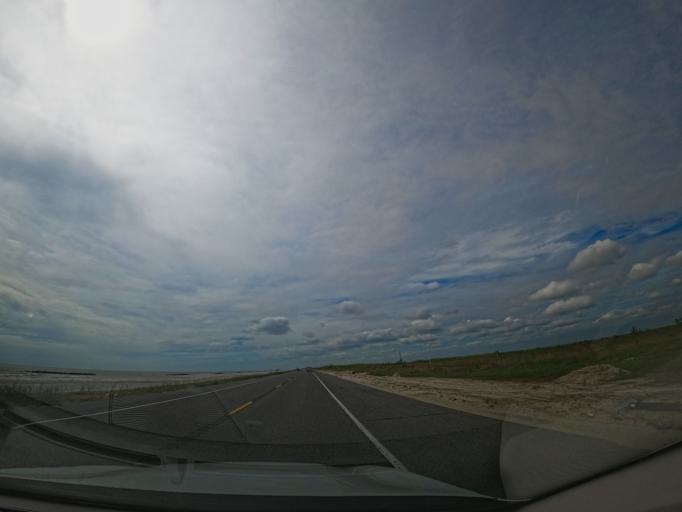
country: US
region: Louisiana
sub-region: Cameron Parish
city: Cameron
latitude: 29.7657
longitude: -93.5278
